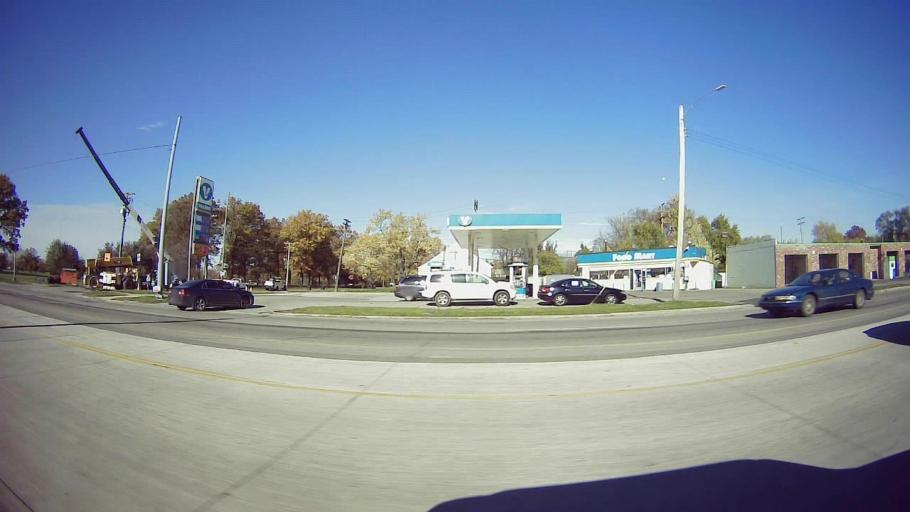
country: US
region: Michigan
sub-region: Wayne County
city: Dearborn Heights
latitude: 42.3573
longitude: -83.2519
